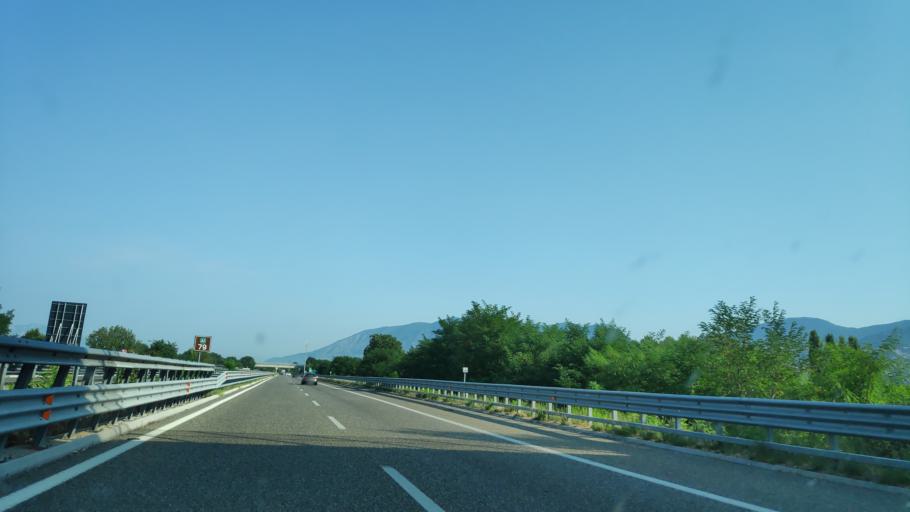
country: IT
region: Campania
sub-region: Provincia di Salerno
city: Padula
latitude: 40.3256
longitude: 15.6359
